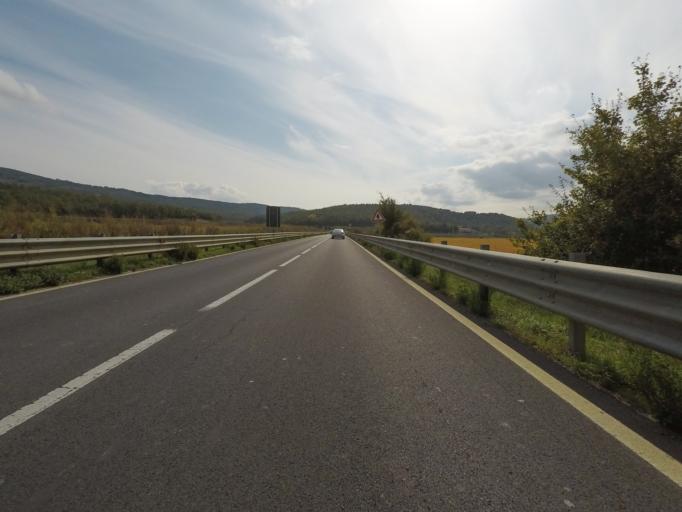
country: IT
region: Tuscany
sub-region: Provincia di Siena
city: Murlo
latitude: 43.1603
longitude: 11.2895
